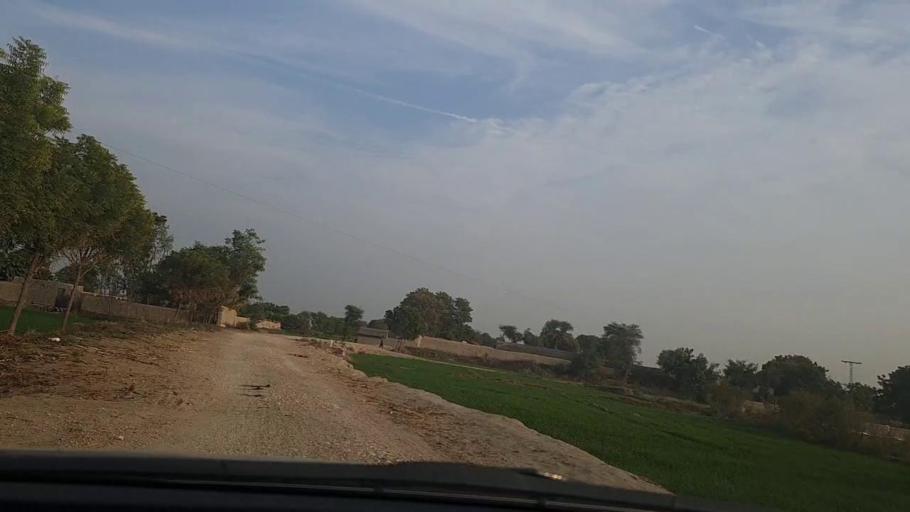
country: PK
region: Sindh
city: Daulatpur
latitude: 26.3321
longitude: 68.0228
